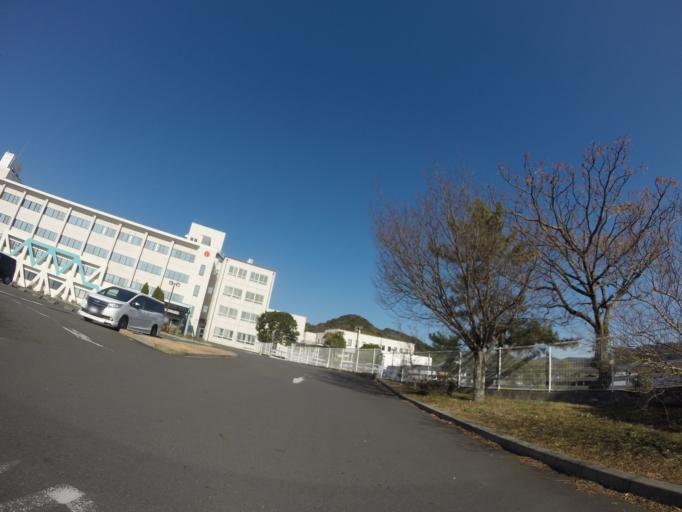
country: JP
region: Shizuoka
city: Shizuoka-shi
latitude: 35.0186
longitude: 138.3982
